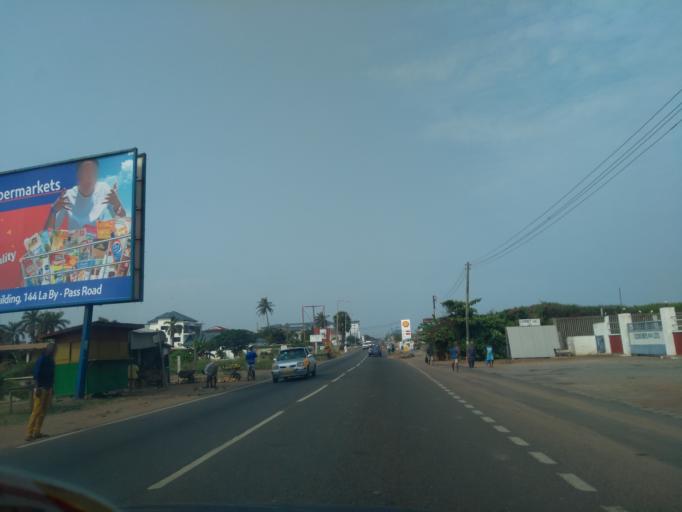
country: GH
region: Greater Accra
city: Accra
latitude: 5.5531
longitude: -0.1760
